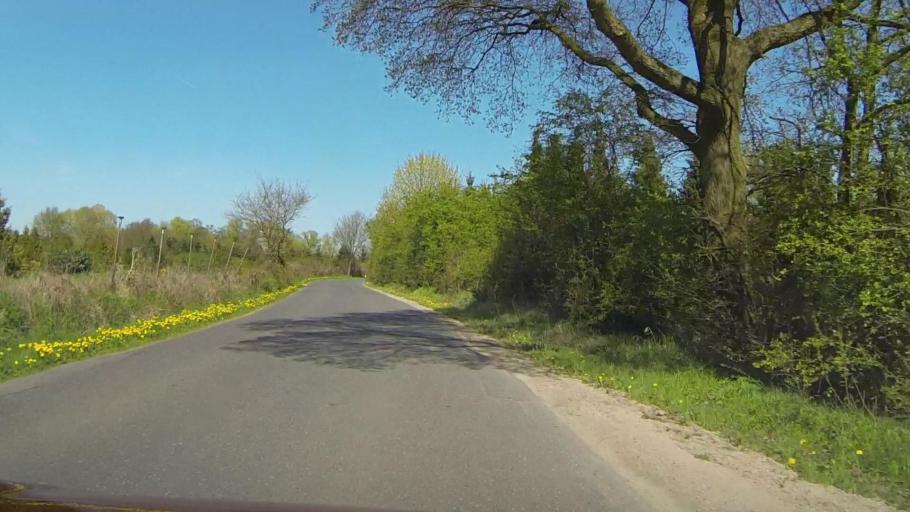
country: DE
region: Schleswig-Holstein
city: Tornesch
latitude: 53.6797
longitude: 9.7102
